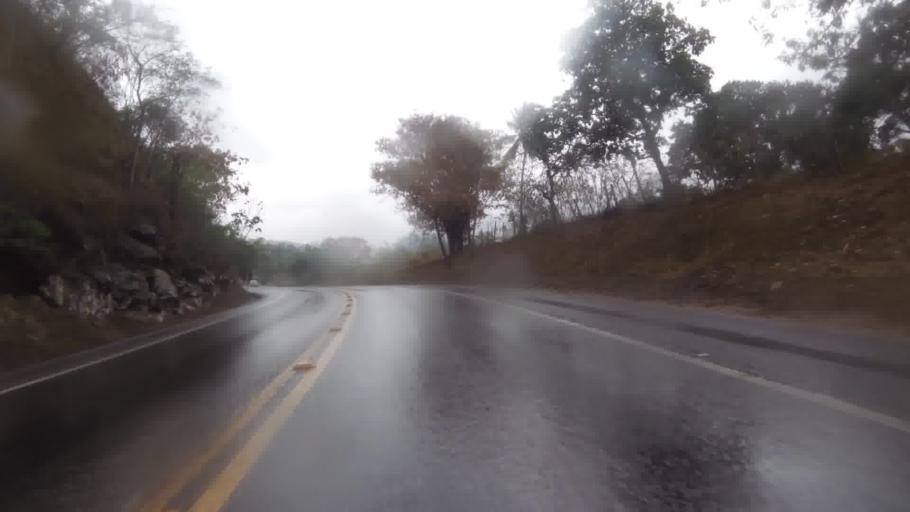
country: BR
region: Espirito Santo
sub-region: Cachoeiro De Itapemirim
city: Cachoeiro de Itapemirim
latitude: -20.9219
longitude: -41.0784
